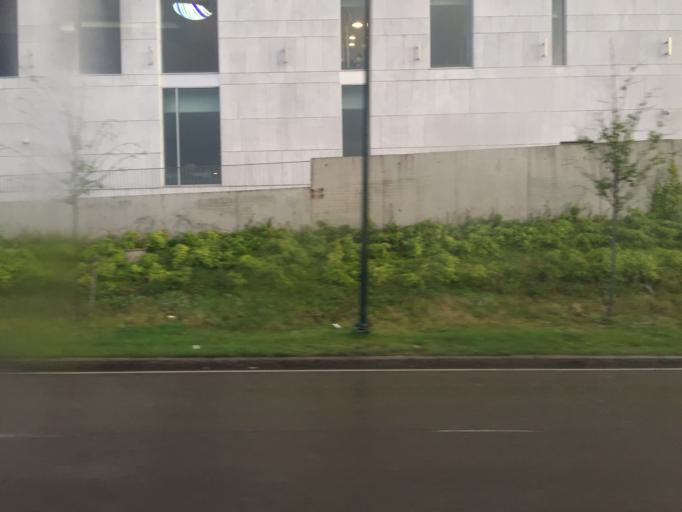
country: NO
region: Akershus
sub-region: Lorenskog
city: Kjenn
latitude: 59.9283
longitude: 10.9619
